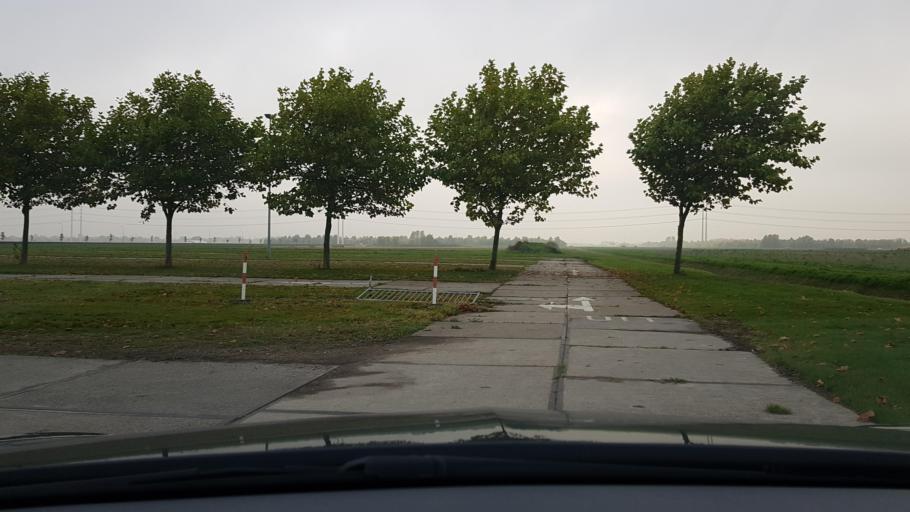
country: NL
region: South Holland
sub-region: Gemeente Hillegom
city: Hillegom
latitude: 52.2873
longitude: 4.6232
